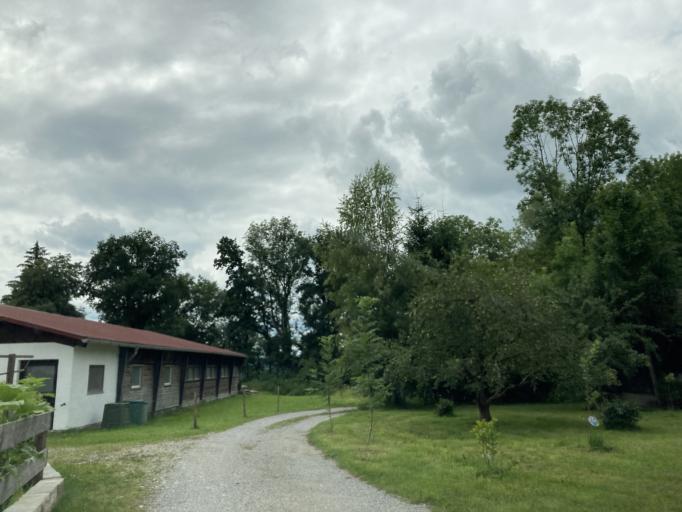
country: DE
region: Bavaria
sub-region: Upper Bavaria
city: Rosenheim
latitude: 47.8797
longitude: 12.1454
